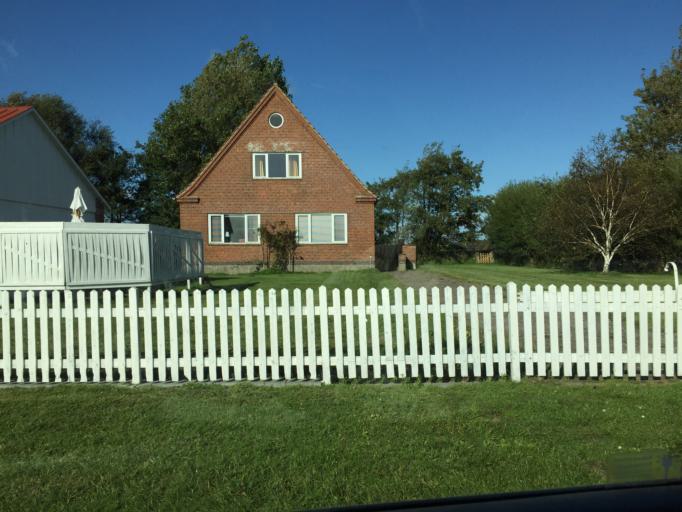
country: DE
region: Schleswig-Holstein
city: Klanxbull
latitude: 54.9553
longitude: 8.6889
